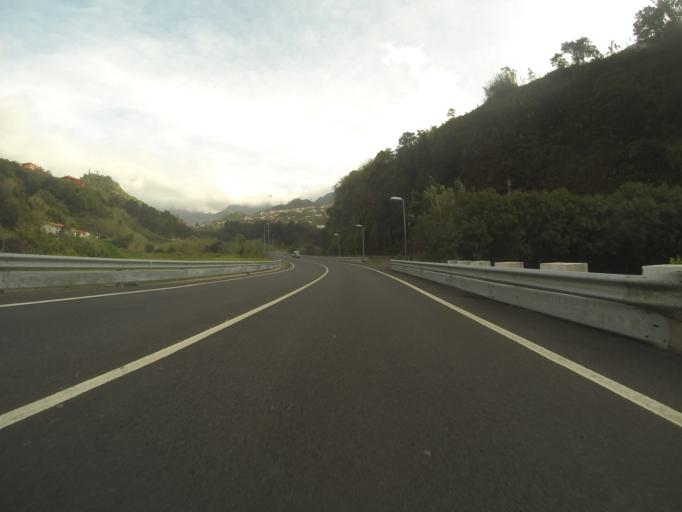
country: PT
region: Madeira
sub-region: Sao Vicente
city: Sao Vicente
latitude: 32.8009
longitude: -17.0434
